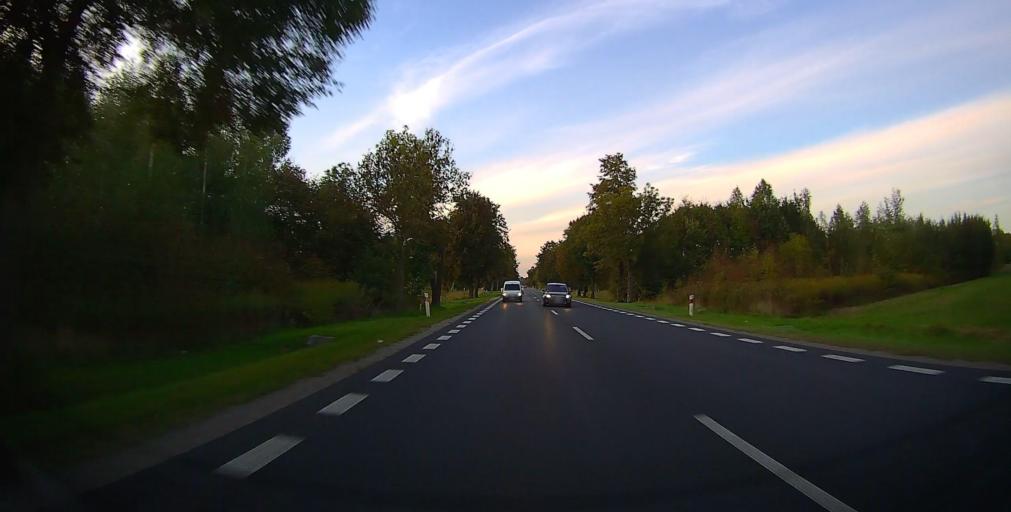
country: PL
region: Masovian Voivodeship
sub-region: Powiat kozienicki
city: Ryczywol
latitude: 51.7419
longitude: 21.3885
